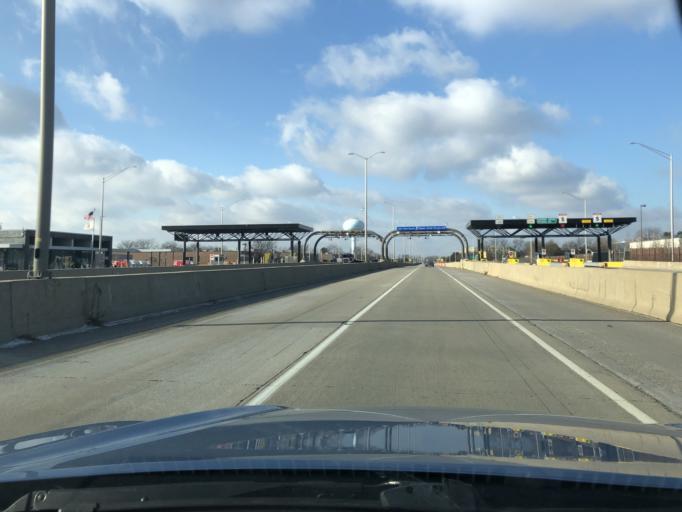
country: US
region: Illinois
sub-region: Lake County
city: Deerfield
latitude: 42.1497
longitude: -87.8538
